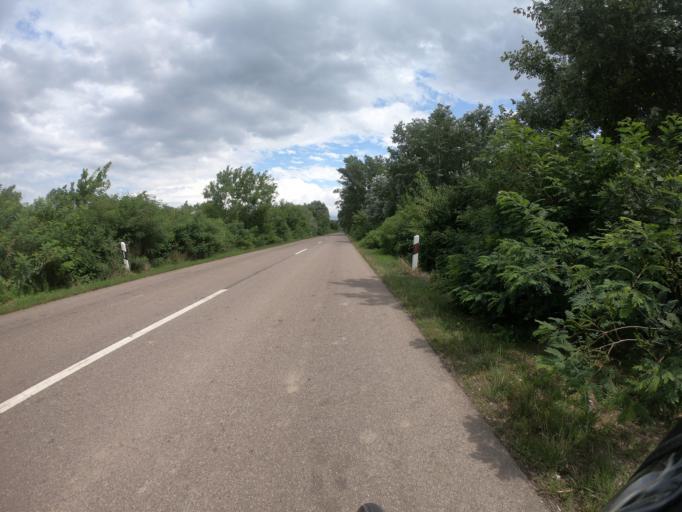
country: HU
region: Jasz-Nagykun-Szolnok
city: Tiszafured
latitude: 47.6907
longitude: 20.7709
